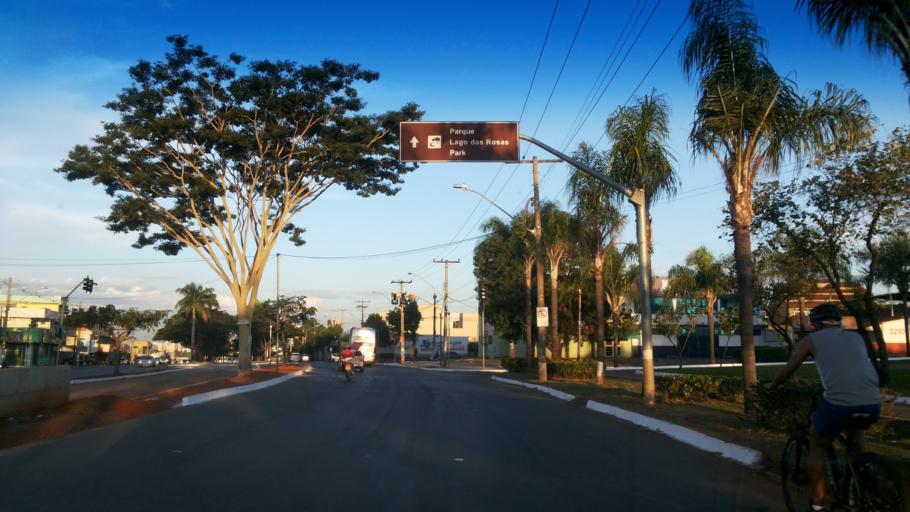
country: BR
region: Goias
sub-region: Goiania
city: Goiania
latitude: -16.6396
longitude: -49.2718
